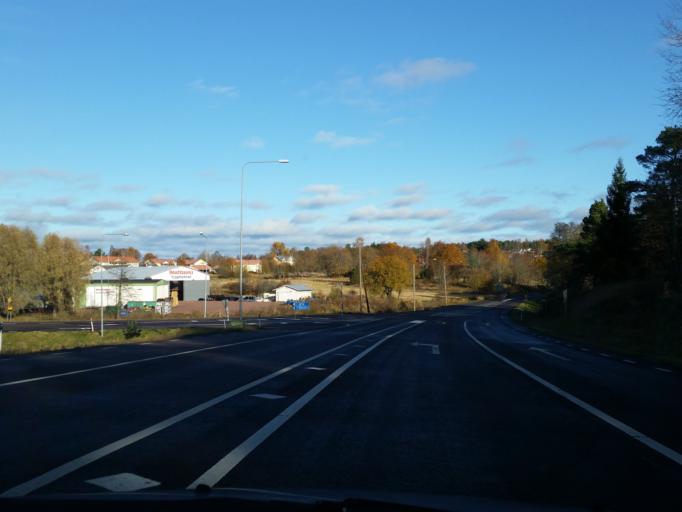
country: AX
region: Alands landsbygd
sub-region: Finstroem
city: Finstroem
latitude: 60.2282
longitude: 19.9895
